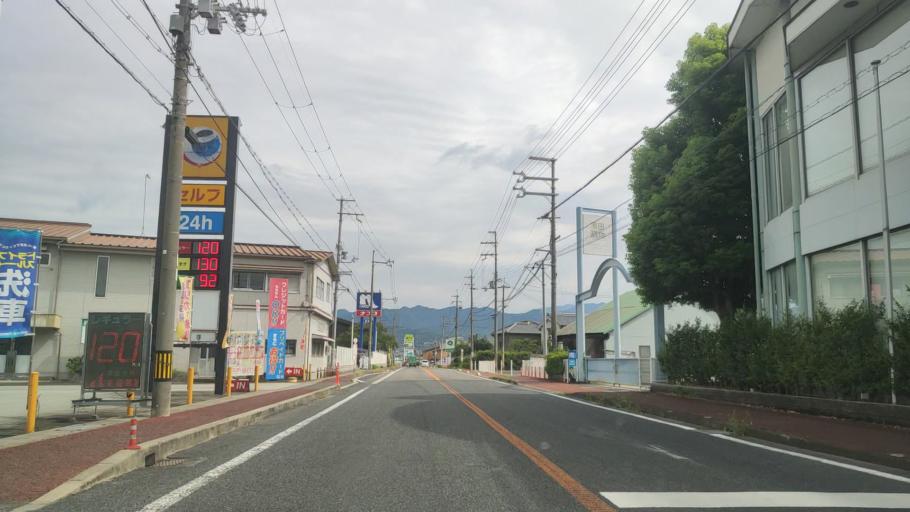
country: JP
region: Wakayama
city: Hashimoto
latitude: 34.3042
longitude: 135.5497
